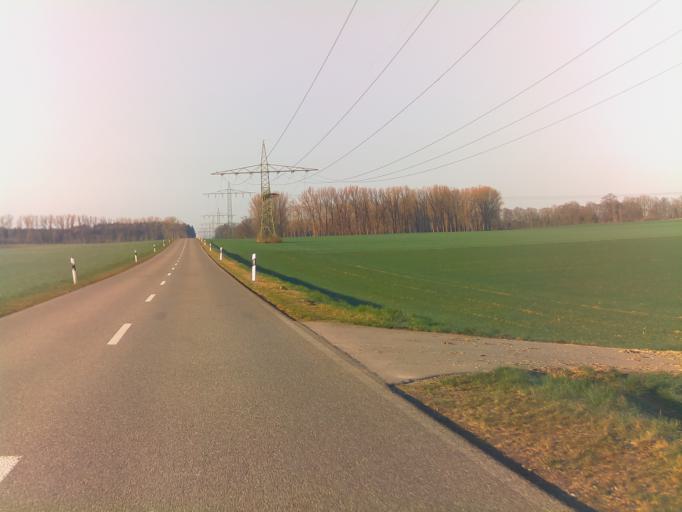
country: DE
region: Bavaria
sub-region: Upper Bavaria
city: Scheuring
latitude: 48.1464
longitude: 10.8787
